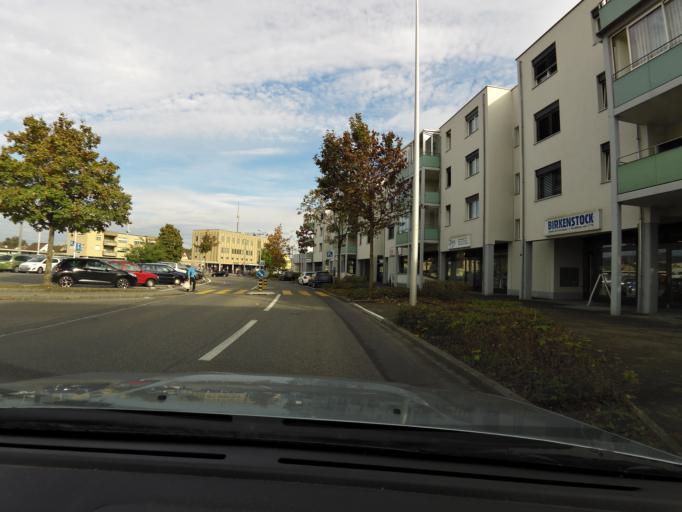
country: CH
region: Aargau
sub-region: Bezirk Lenzburg
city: Lenzburg
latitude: 47.3907
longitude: 8.1686
